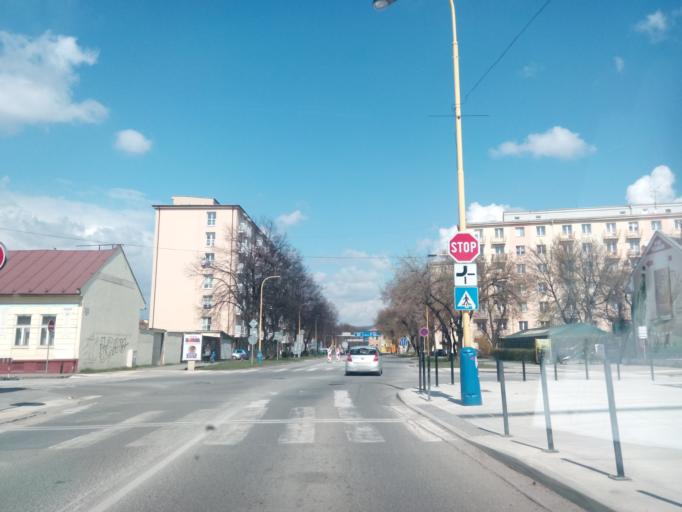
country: SK
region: Kosicky
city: Kosice
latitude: 48.7141
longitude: 21.2545
